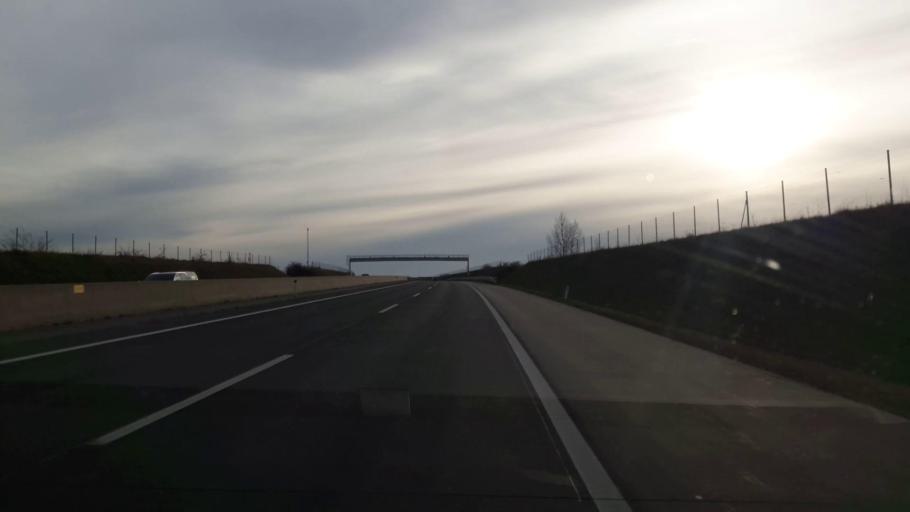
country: AT
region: Lower Austria
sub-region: Politischer Bezirk Mistelbach
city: Hochleithen
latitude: 48.4615
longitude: 16.5532
